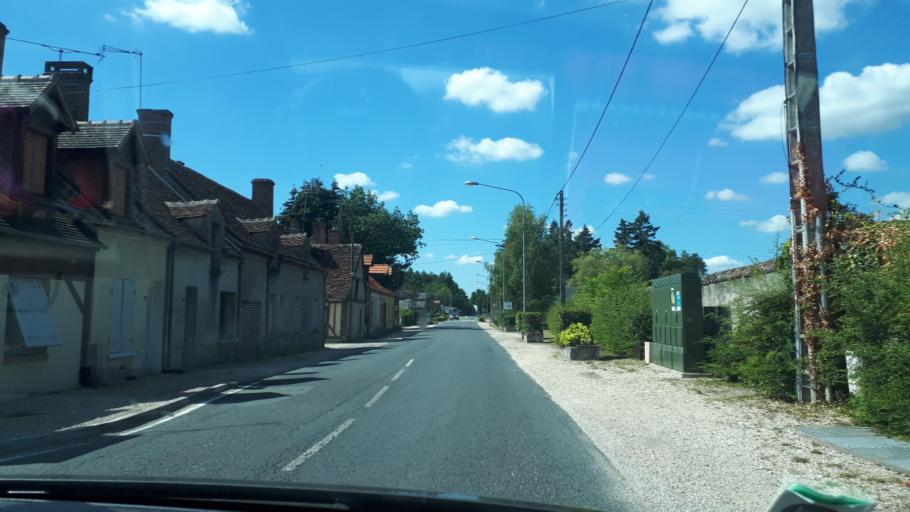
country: FR
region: Centre
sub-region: Departement du Loir-et-Cher
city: Neung-sur-Beuvron
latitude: 47.5413
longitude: 1.8473
